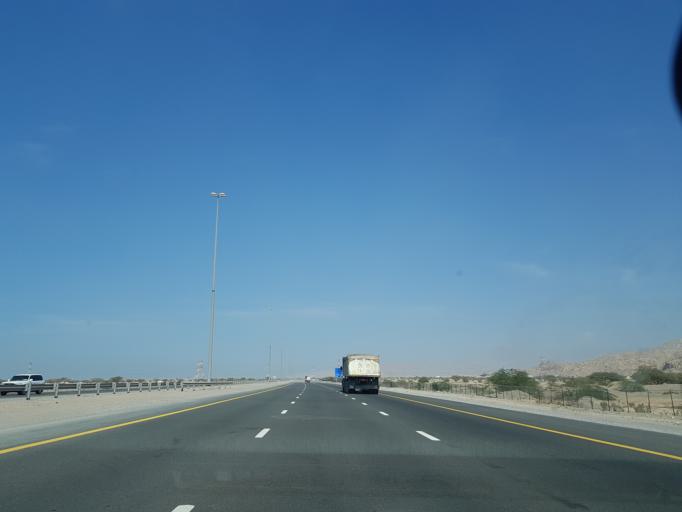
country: AE
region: Ra's al Khaymah
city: Ras al-Khaimah
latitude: 25.7356
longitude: 56.0154
